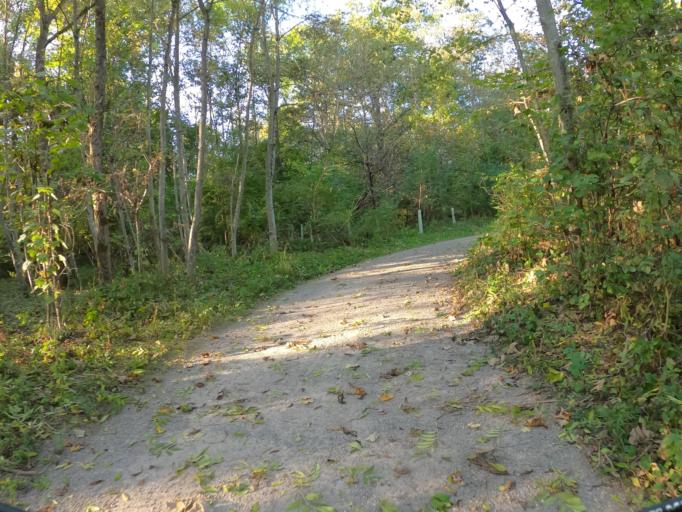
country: DE
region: Bavaria
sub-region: Swabia
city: Nersingen
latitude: 48.4440
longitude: 10.1309
